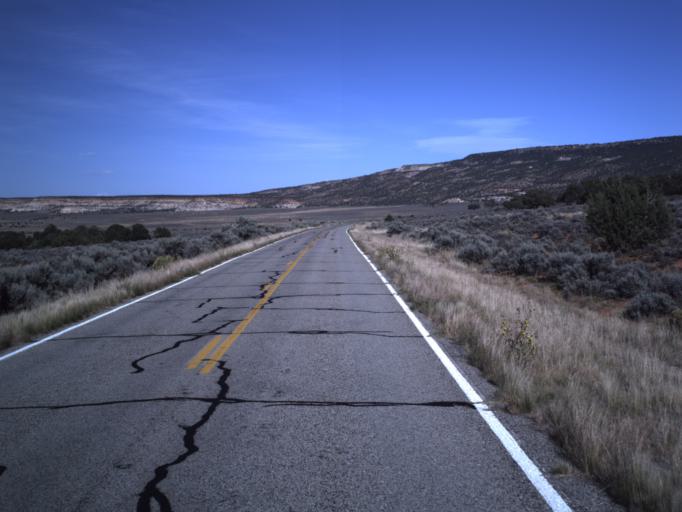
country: US
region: Utah
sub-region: San Juan County
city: Monticello
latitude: 38.0040
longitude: -109.4550
